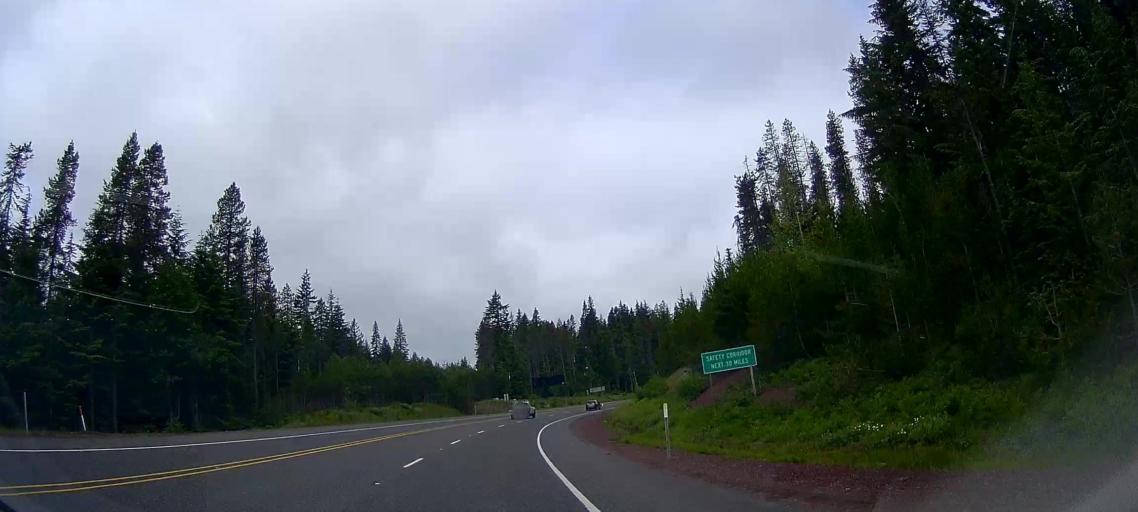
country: US
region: Oregon
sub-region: Clackamas County
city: Mount Hood Village
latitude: 45.2840
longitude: -121.7228
